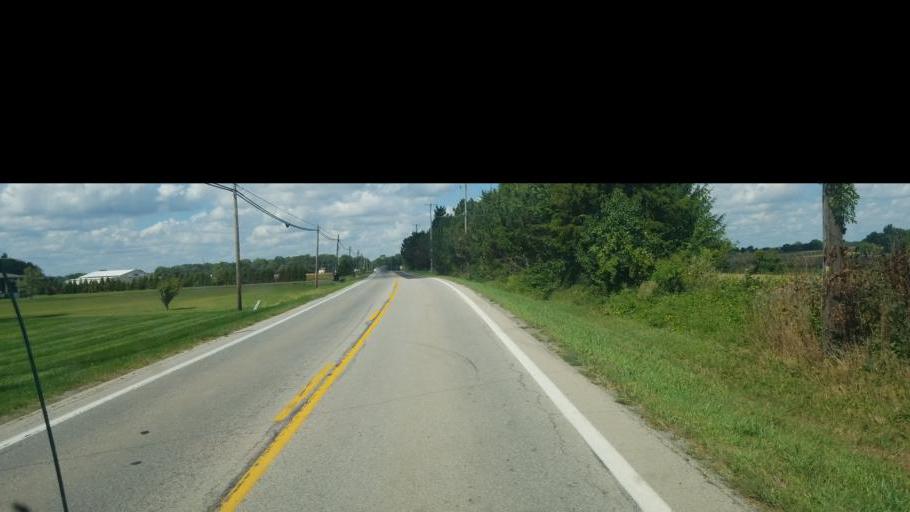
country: US
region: Ohio
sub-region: Marion County
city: Marion
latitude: 40.5419
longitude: -83.1105
